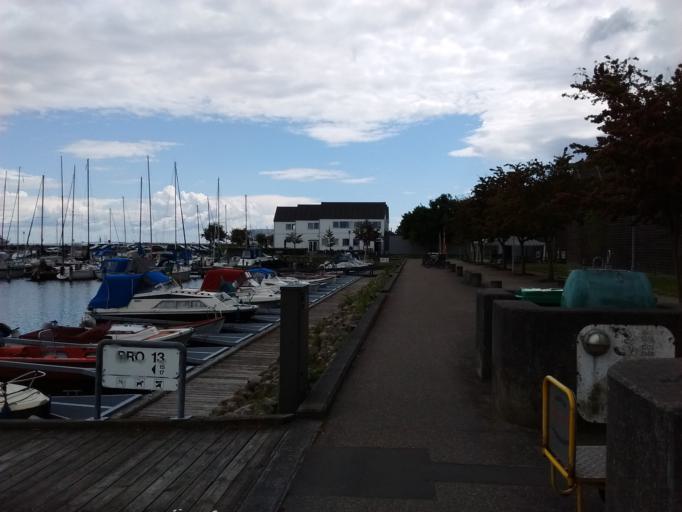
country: DK
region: Capital Region
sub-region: Dragor Kommune
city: Dragor
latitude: 55.6416
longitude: 12.6512
